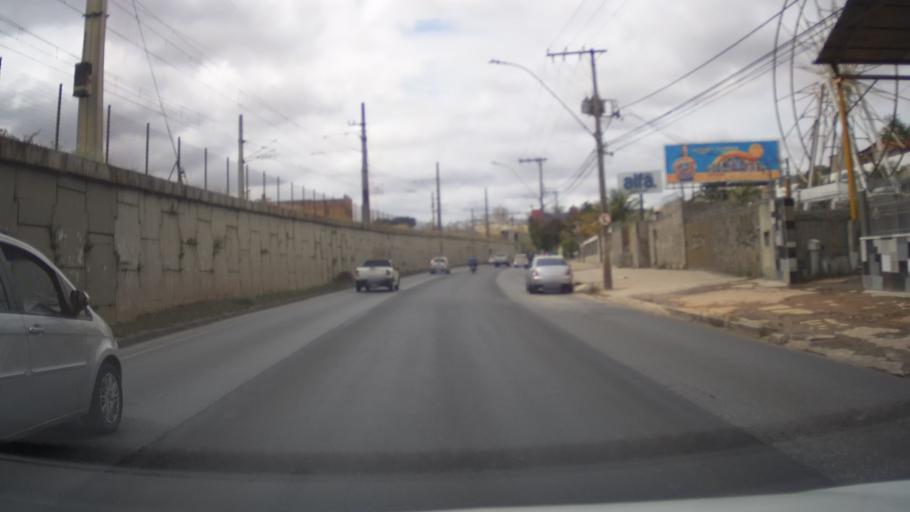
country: BR
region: Minas Gerais
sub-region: Belo Horizonte
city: Belo Horizonte
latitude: -19.8315
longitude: -43.9411
